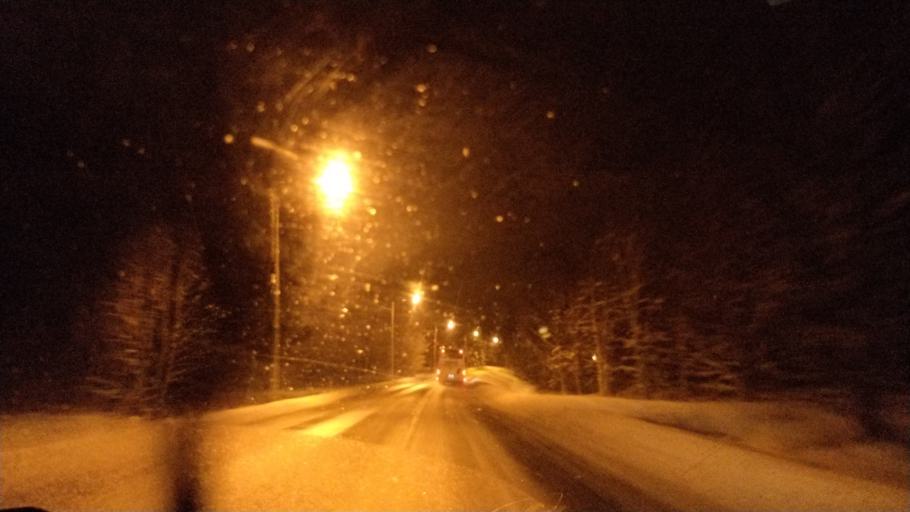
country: FI
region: Lapland
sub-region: Rovaniemi
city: Rovaniemi
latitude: 66.2920
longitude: 25.3501
